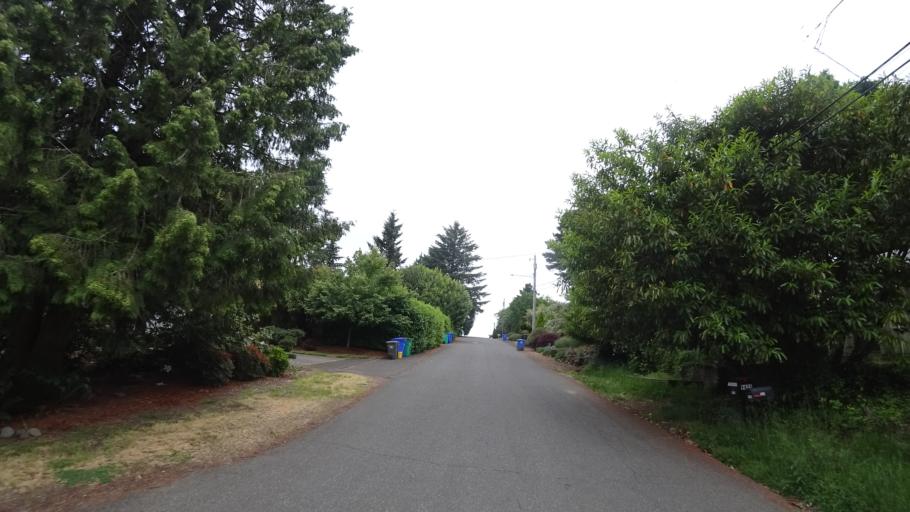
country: US
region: Oregon
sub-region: Clackamas County
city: Lake Oswego
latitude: 45.4563
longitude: -122.6809
